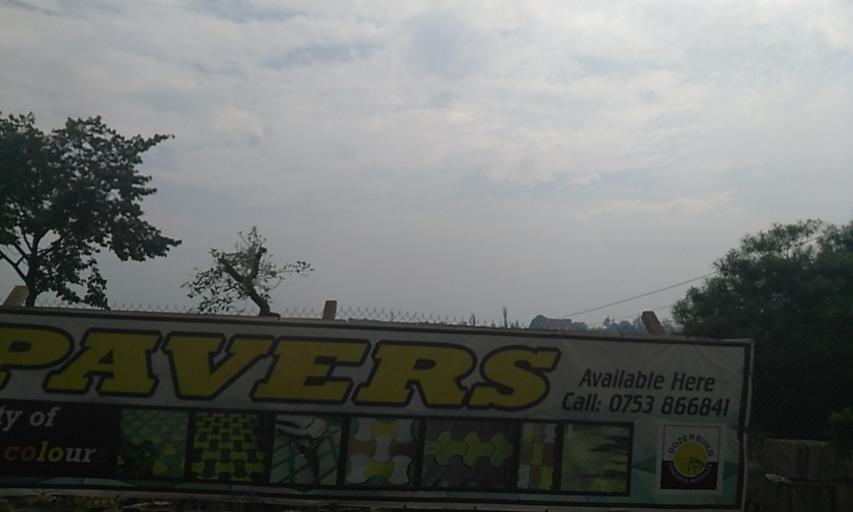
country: UG
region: Central Region
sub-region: Kampala District
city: Kampala
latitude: 0.3024
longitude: 32.5584
